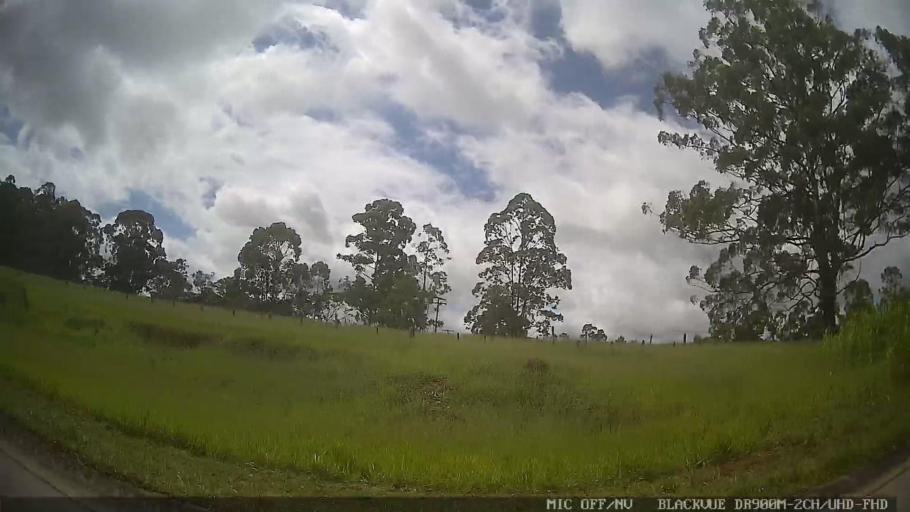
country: BR
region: Sao Paulo
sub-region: Braganca Paulista
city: Braganca Paulista
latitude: -22.8078
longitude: -46.5356
